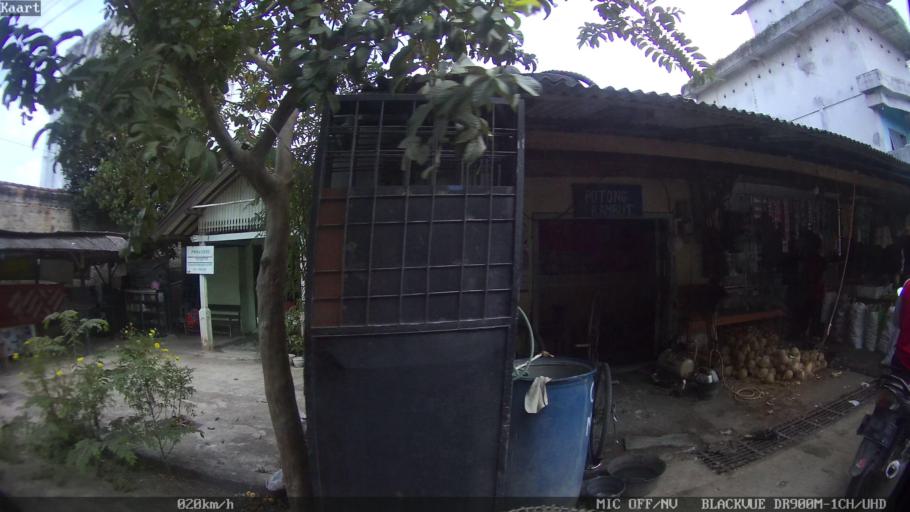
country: ID
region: Lampung
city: Pringsewu
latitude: -5.3584
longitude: 104.9699
